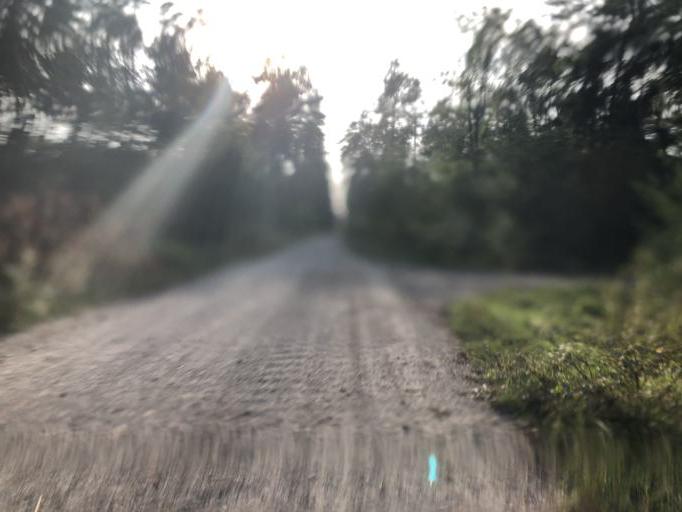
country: DE
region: Bavaria
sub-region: Regierungsbezirk Mittelfranken
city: Uttenreuth
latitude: 49.5789
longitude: 11.0827
